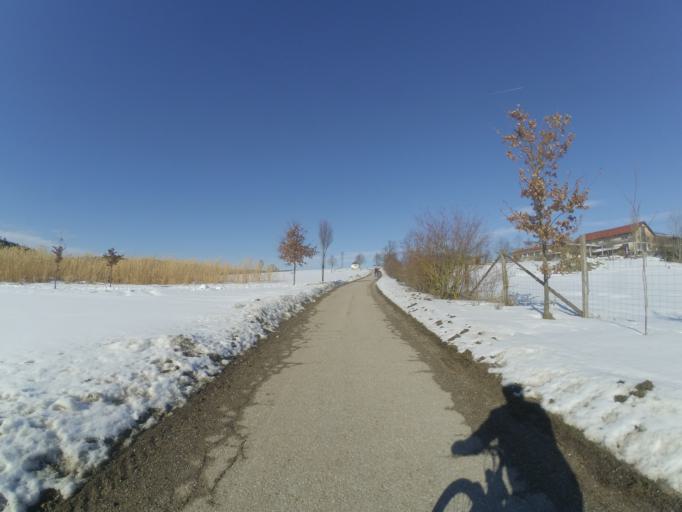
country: DE
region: Bavaria
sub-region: Upper Bavaria
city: Feldkirchen-Westerham
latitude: 47.9290
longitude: 11.8118
